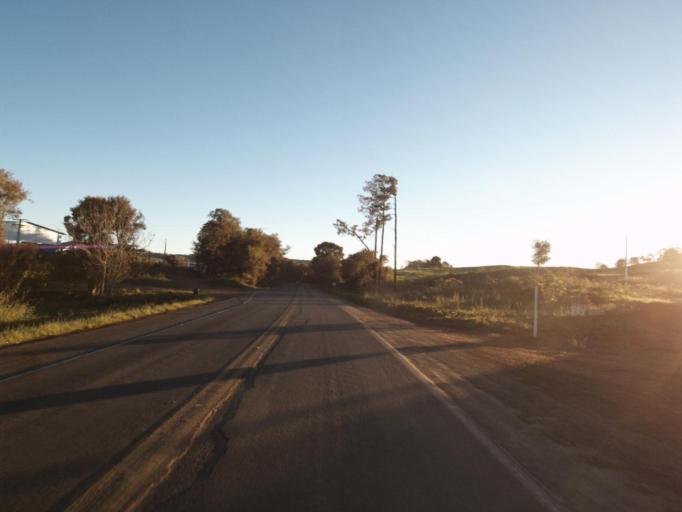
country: BR
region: Santa Catarina
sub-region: Sao Lourenco Do Oeste
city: Sao Lourenco dOeste
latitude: -26.8260
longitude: -53.0948
